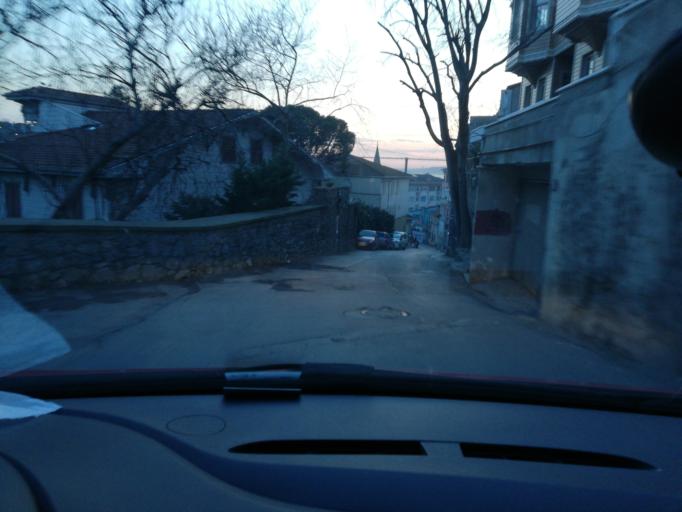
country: TR
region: Istanbul
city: UEskuedar
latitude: 41.0513
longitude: 29.0556
